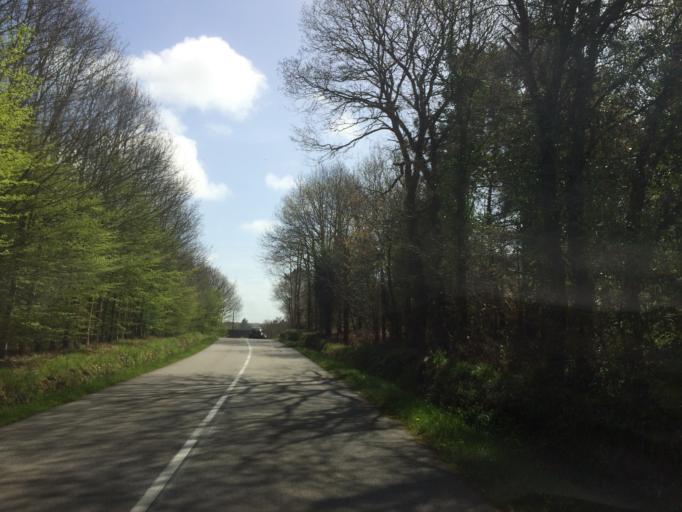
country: FR
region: Brittany
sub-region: Departement du Morbihan
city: Ploemel
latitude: 47.6345
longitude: -3.0477
